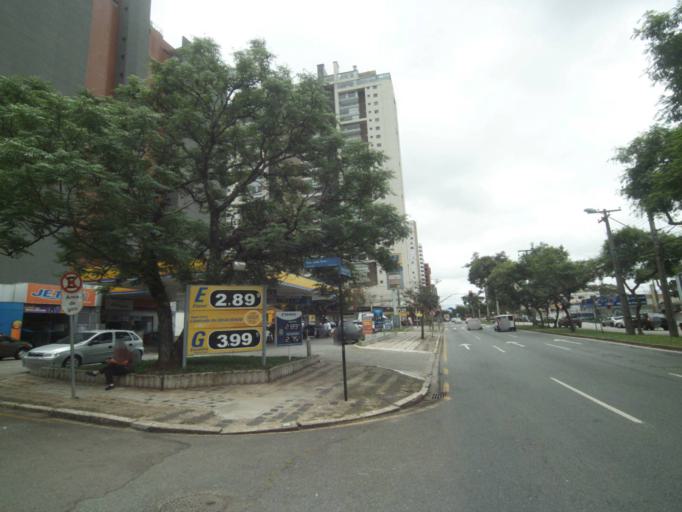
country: BR
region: Parana
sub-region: Curitiba
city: Curitiba
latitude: -25.4453
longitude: -49.2825
